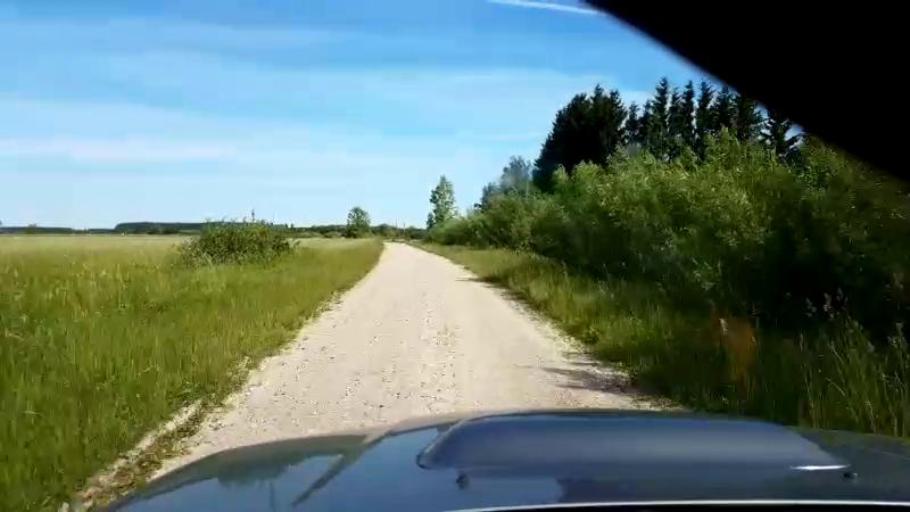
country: EE
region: Paernumaa
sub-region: Sauga vald
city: Sauga
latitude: 58.4893
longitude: 24.5306
